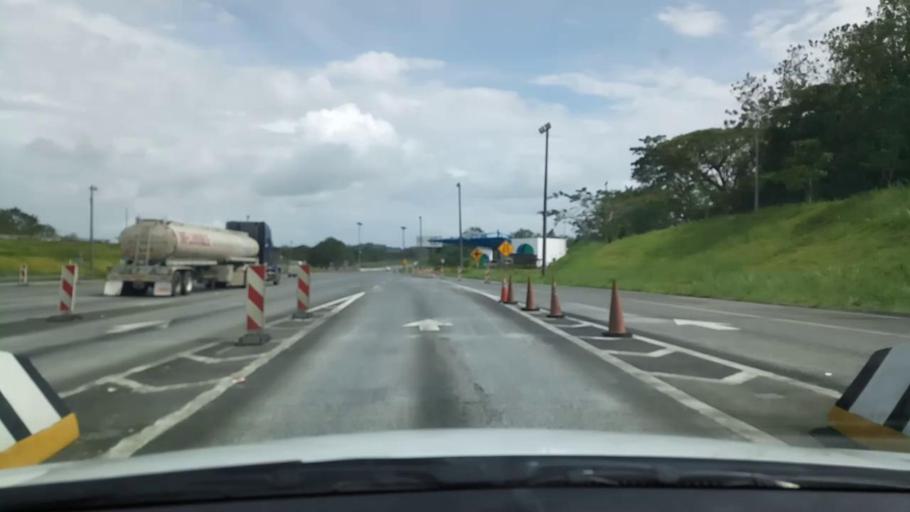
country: PA
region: Colon
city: Buena Vista
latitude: 9.2628
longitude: -79.7003
